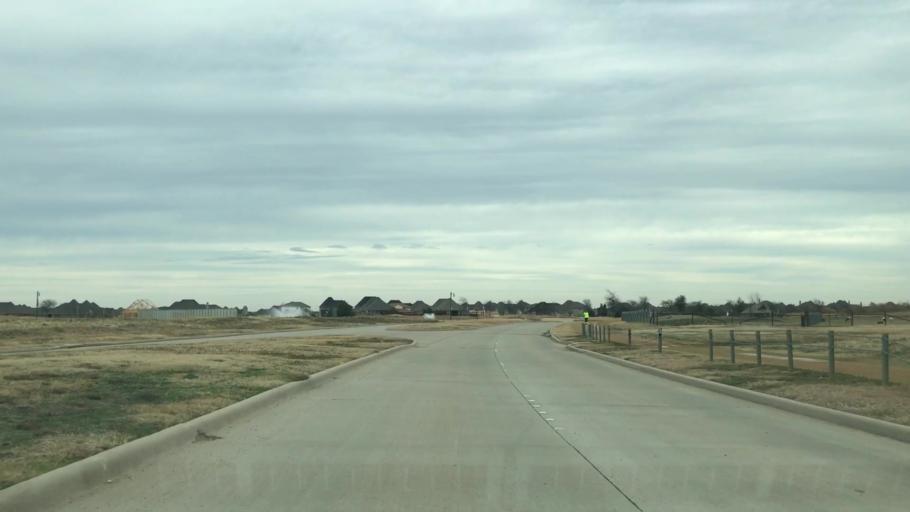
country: US
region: Texas
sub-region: Denton County
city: The Colony
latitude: 33.1032
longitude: -96.9264
